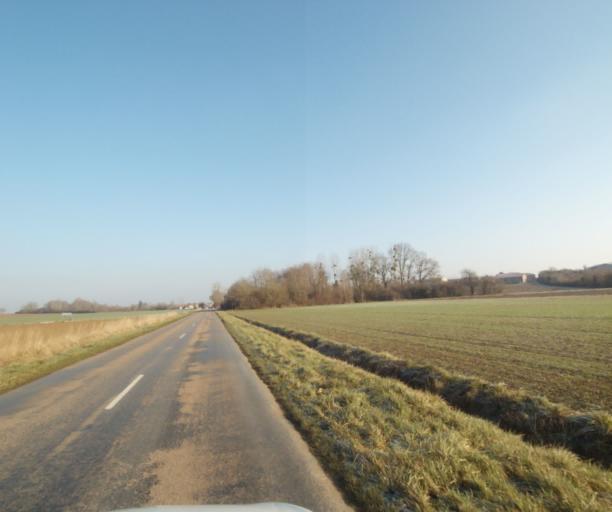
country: FR
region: Champagne-Ardenne
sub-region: Departement de la Haute-Marne
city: Montier-en-Der
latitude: 48.4487
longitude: 4.7639
